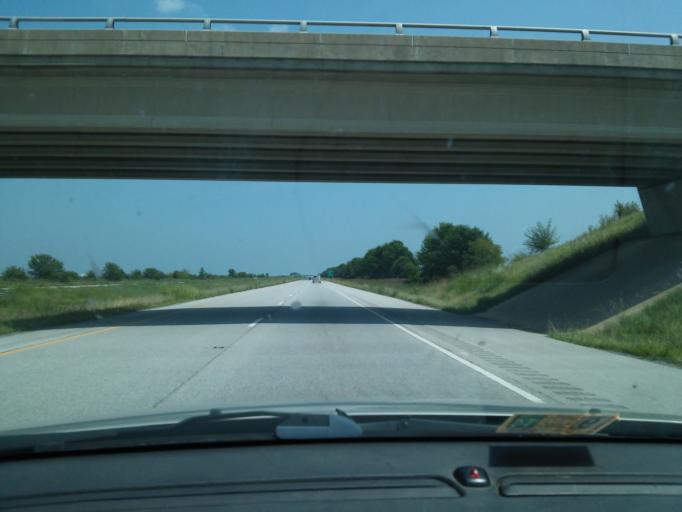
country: US
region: Illinois
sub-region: Scott County
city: Winchester
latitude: 39.6802
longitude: -90.3470
